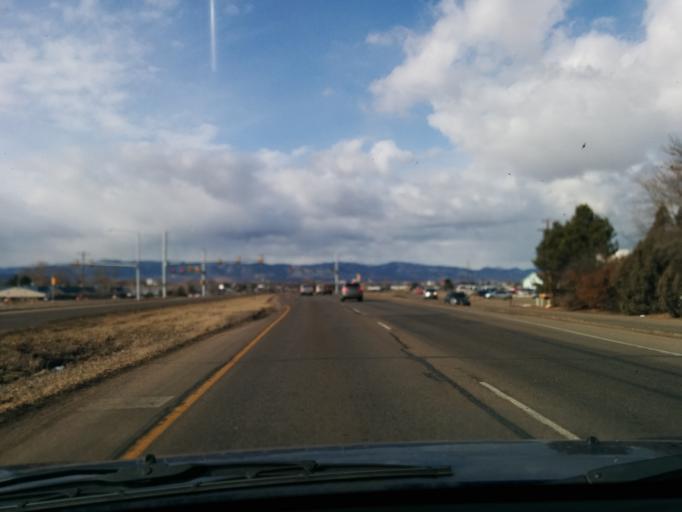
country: US
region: Colorado
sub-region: Larimer County
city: Fort Collins
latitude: 40.5814
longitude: -105.0256
